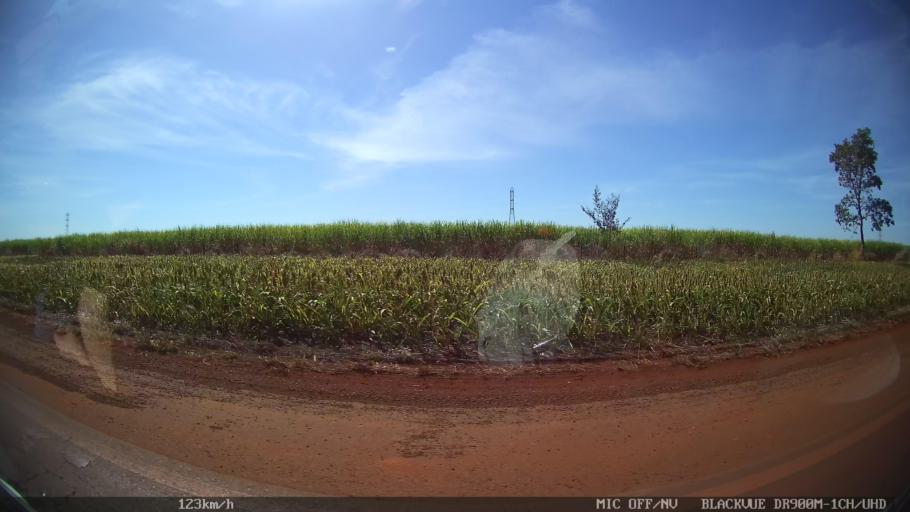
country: BR
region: Sao Paulo
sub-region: Ipua
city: Ipua
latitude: -20.4652
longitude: -48.1282
